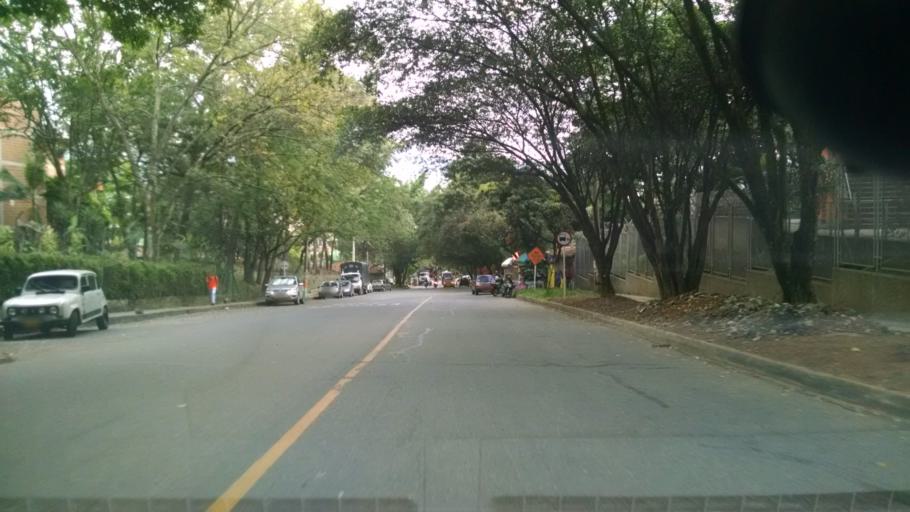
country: CO
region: Antioquia
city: Medellin
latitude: 6.2811
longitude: -75.5846
